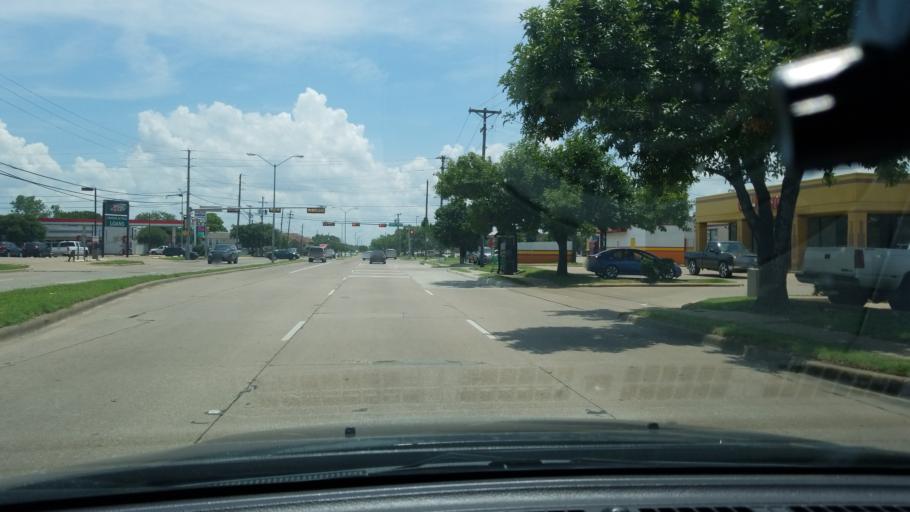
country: US
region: Texas
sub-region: Dallas County
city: Balch Springs
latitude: 32.7350
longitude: -96.6485
